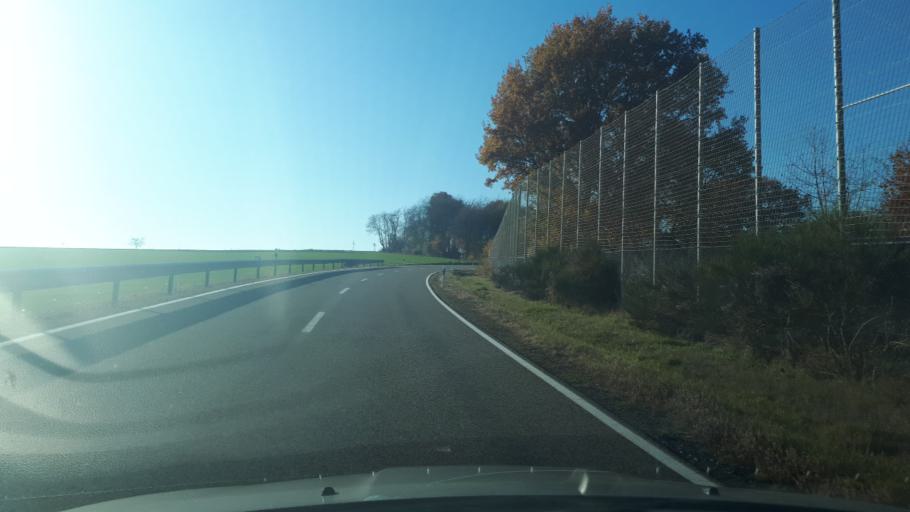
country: DE
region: Rheinland-Pfalz
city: Weiler
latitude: 50.1462
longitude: 7.0736
